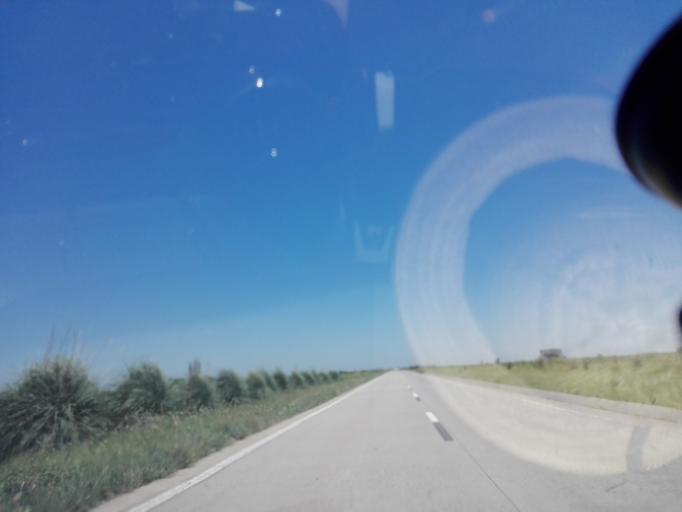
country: AR
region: Cordoba
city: Leones
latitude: -32.6067
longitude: -62.4222
